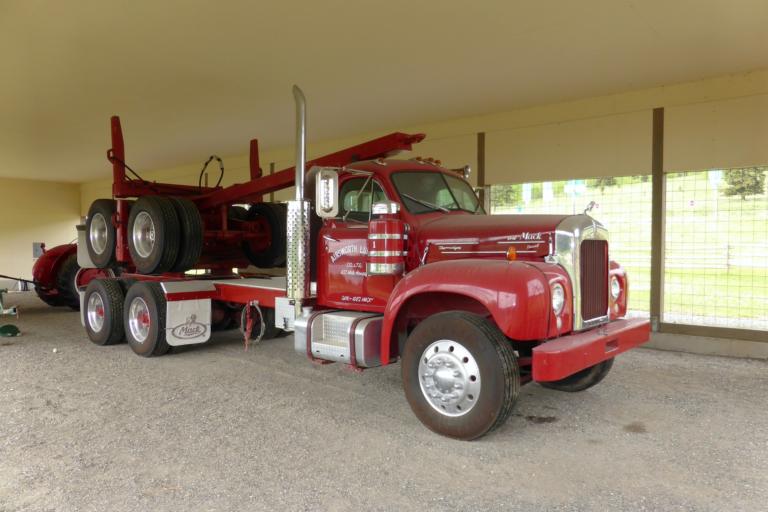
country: CA
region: British Columbia
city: Williams Lake
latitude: 51.7501
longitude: -121.3493
